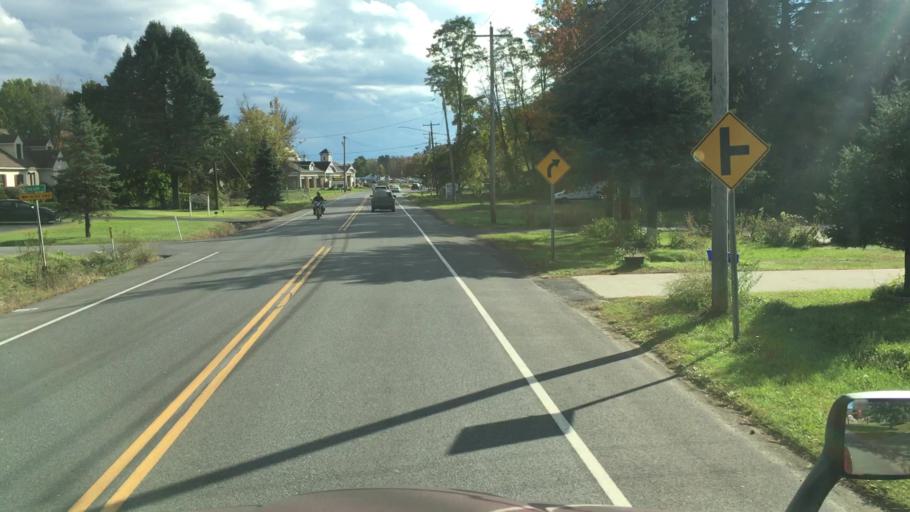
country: US
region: New York
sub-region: Schenectady County
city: East Glenville
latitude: 42.8642
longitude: -73.9329
